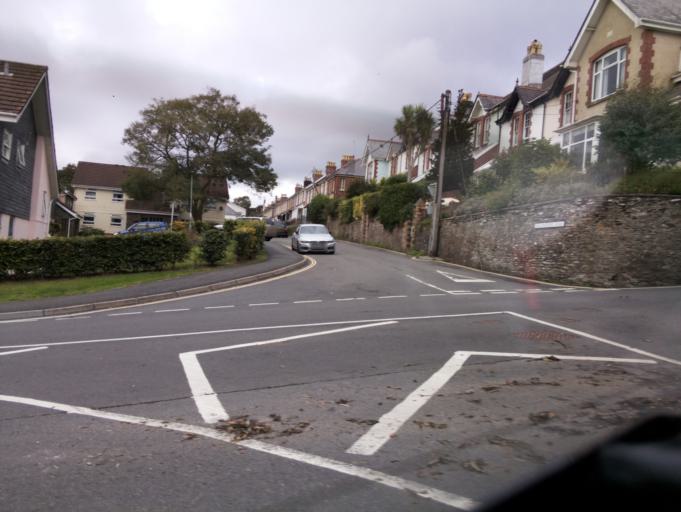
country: GB
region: England
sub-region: Devon
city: Kingsbridge
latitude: 50.2871
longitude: -3.7745
